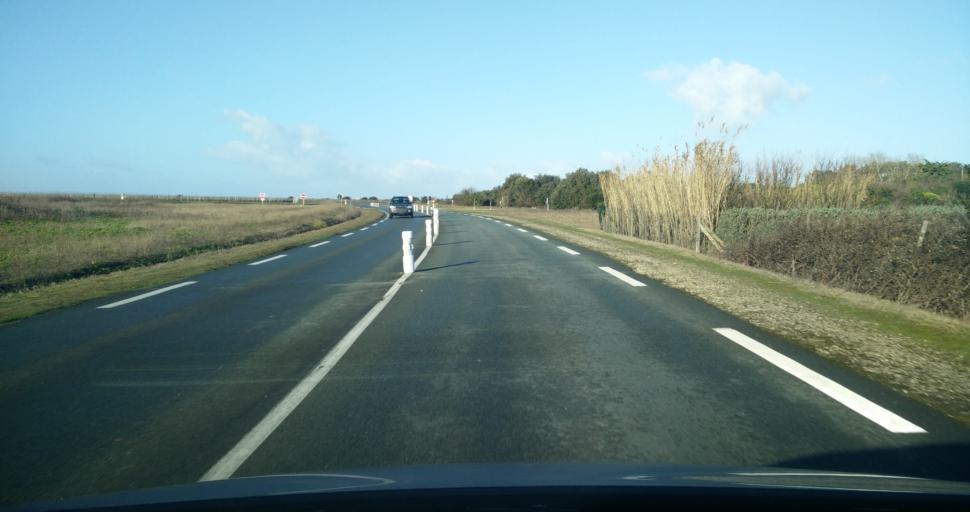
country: FR
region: Poitou-Charentes
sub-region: Departement de la Charente-Maritime
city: Rivedoux-Plage
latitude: 46.1526
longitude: -1.2807
